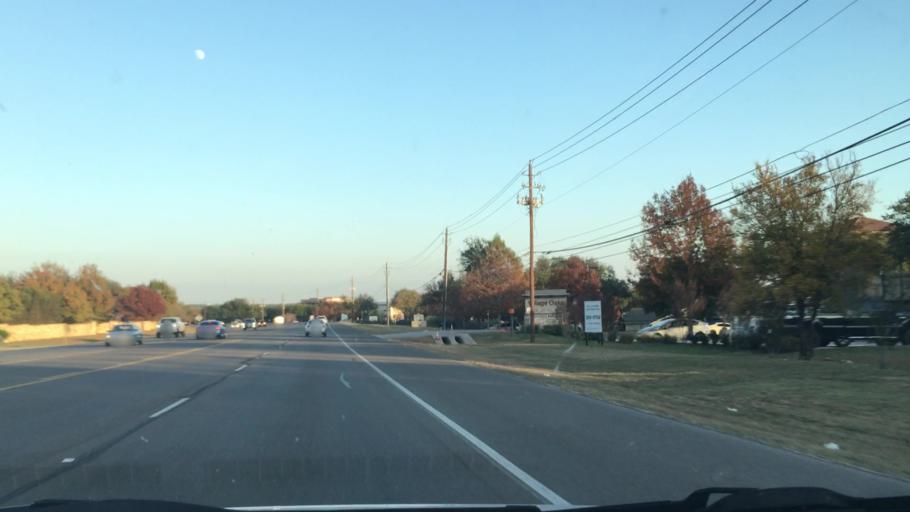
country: US
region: Texas
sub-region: Travis County
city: Bee Cave
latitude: 30.3084
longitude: -97.9245
